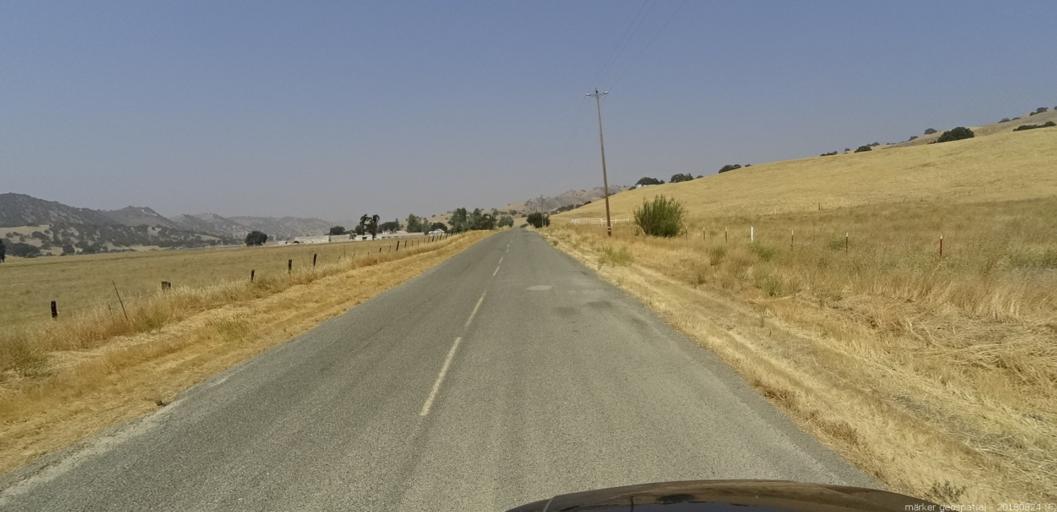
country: US
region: California
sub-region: Monterey County
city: King City
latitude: 36.1828
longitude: -120.8004
